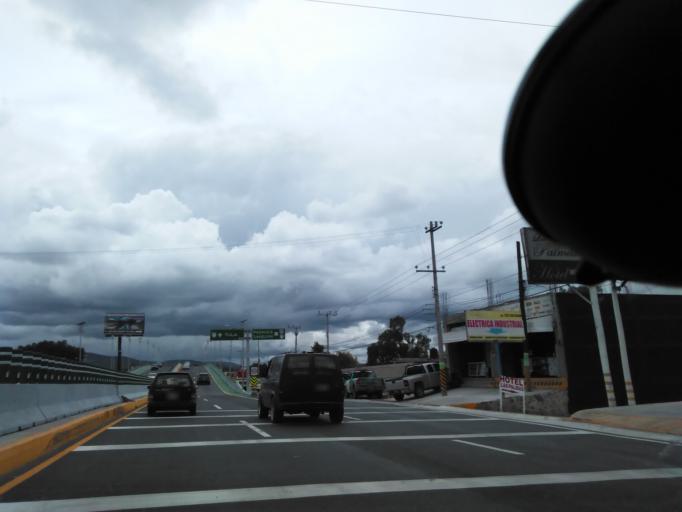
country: MX
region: Hidalgo
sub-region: Tula de Allende
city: Residencial Arboledas
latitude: 20.0543
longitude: -99.3087
